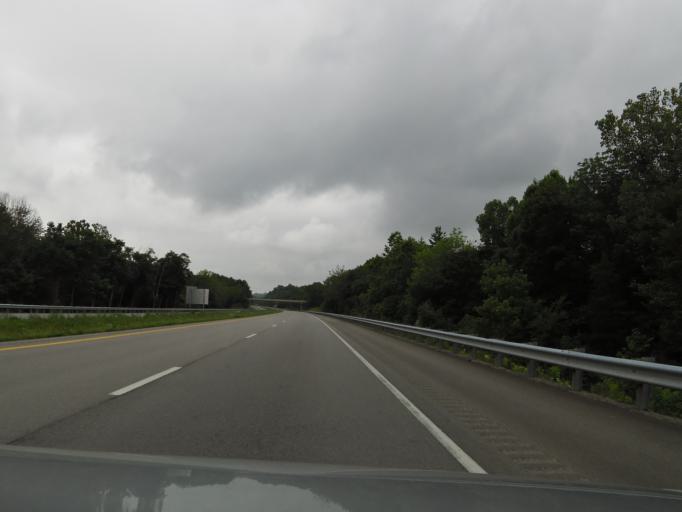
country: US
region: Kentucky
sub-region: Grayson County
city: Leitchfield
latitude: 37.4084
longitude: -86.4644
